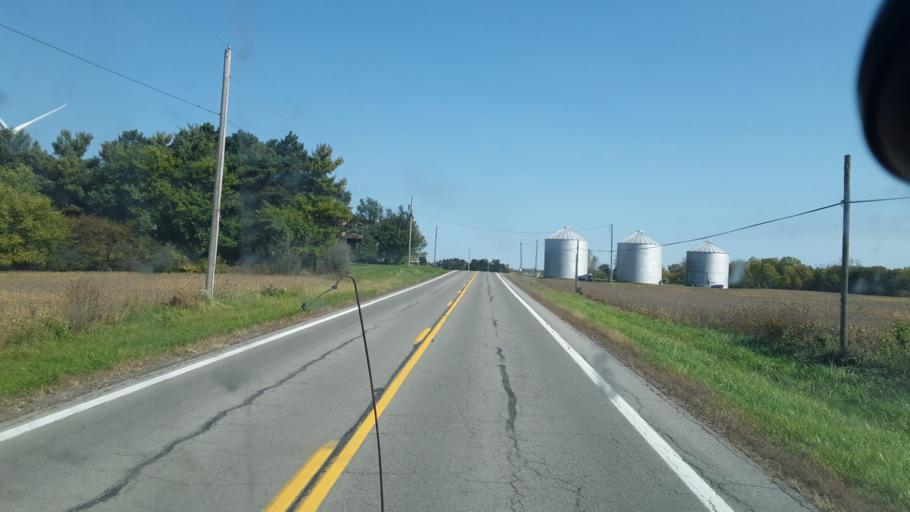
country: US
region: Ohio
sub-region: Logan County
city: Northwood
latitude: 40.5037
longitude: -83.7067
